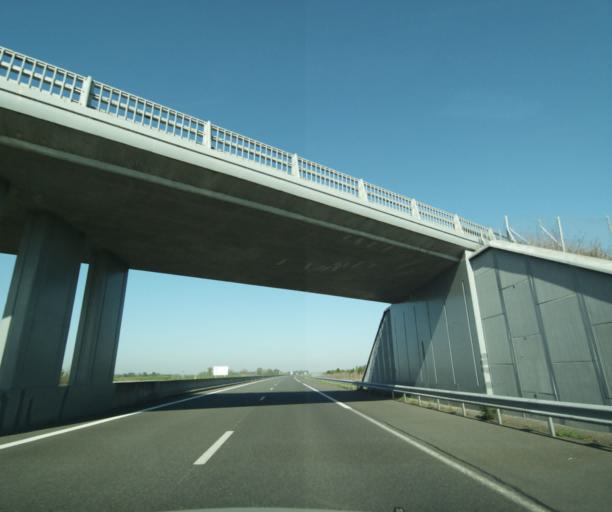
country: FR
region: Centre
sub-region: Departement du Loiret
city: Corbeilles
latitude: 48.0789
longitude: 2.6203
